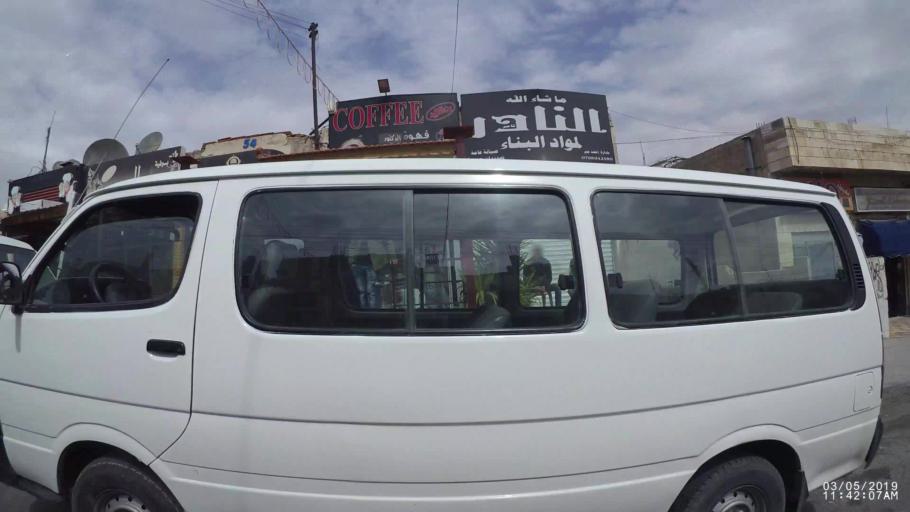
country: JO
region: Amman
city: Amman
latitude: 31.9619
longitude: 35.9540
